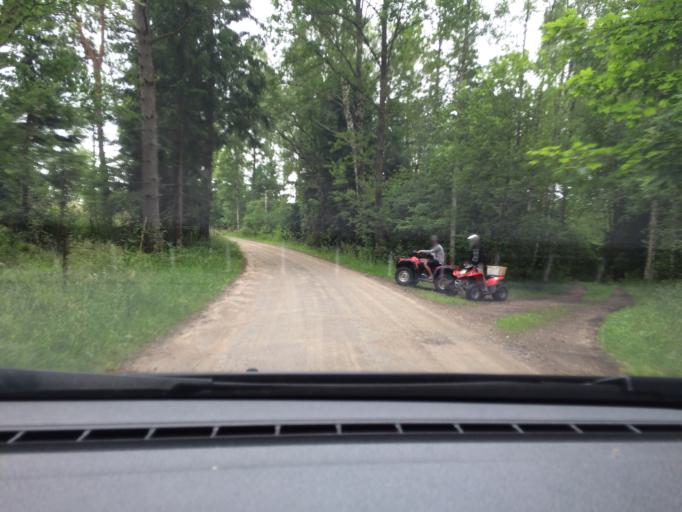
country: SE
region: Joenkoeping
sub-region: Varnamo Kommun
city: Forsheda
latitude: 57.0693
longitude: 13.8007
